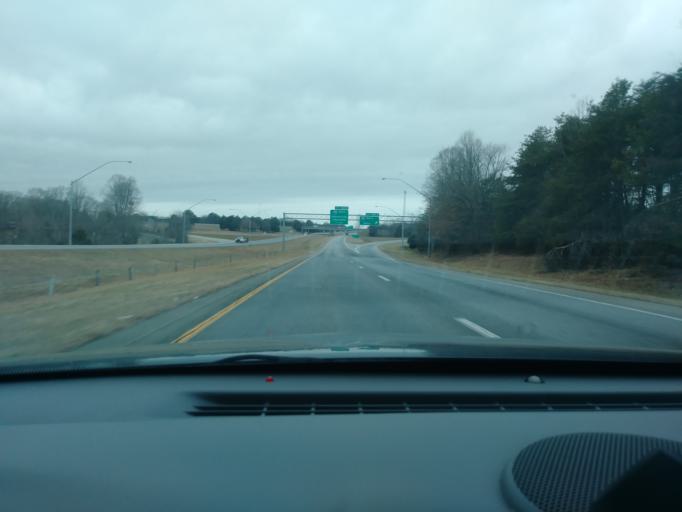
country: US
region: North Carolina
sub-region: Yadkin County
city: Jonesville
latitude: 36.1203
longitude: -80.8078
